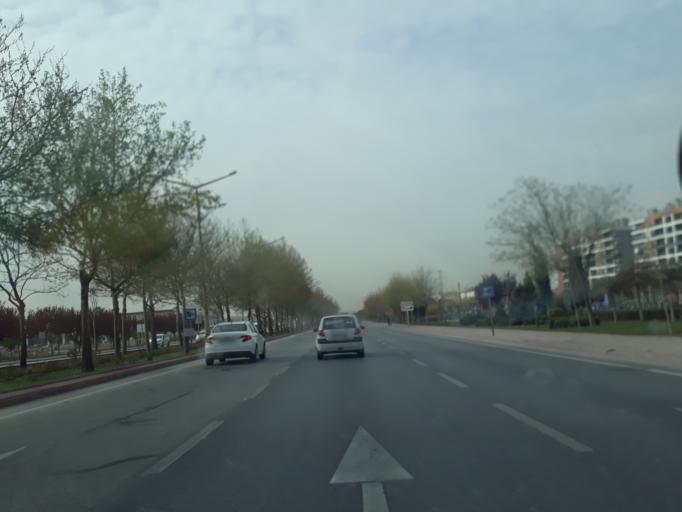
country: TR
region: Konya
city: Selcuklu
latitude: 37.9728
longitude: 32.5159
